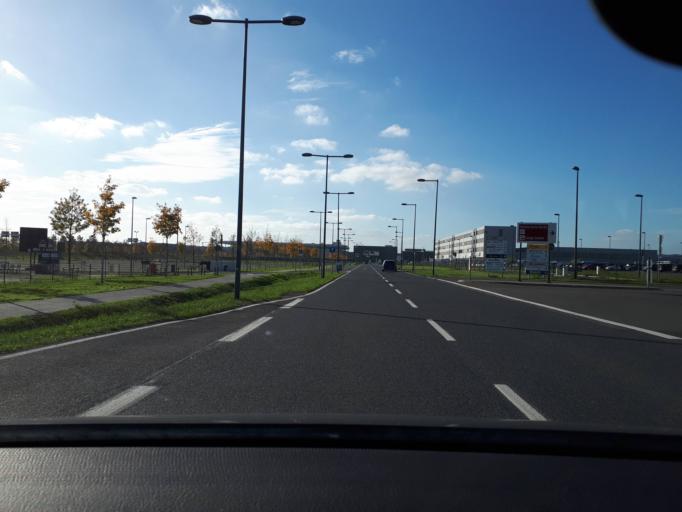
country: DE
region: Brandenburg
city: Schonefeld
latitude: 52.3689
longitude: 13.5233
